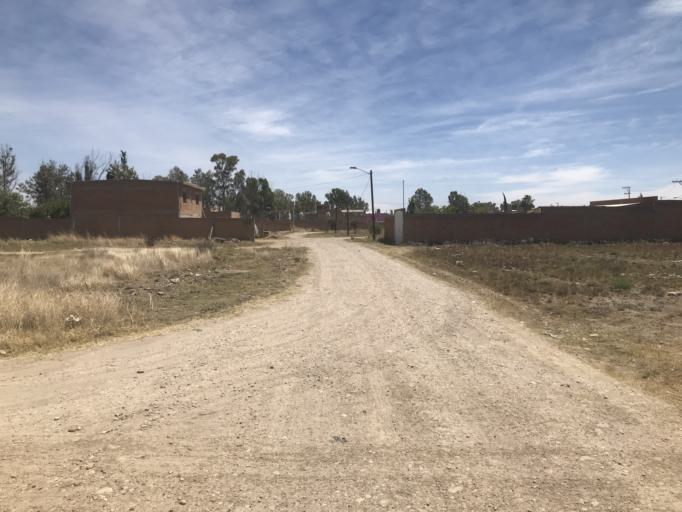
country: MX
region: Durango
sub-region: Durango
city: Sebastian Lerdo de Tejada
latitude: 23.9822
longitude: -104.6554
